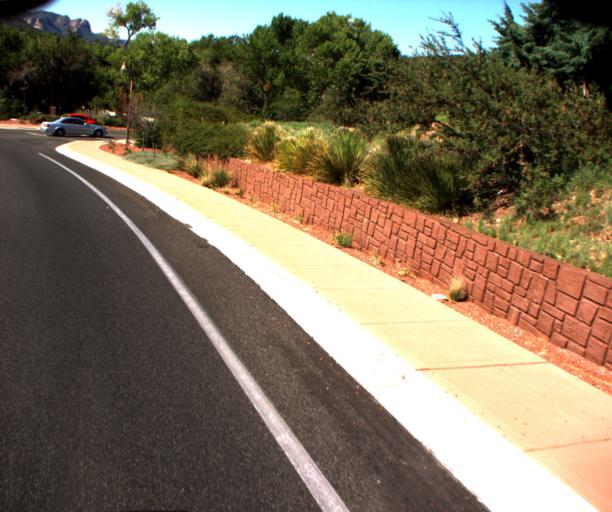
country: US
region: Arizona
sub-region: Coconino County
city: Sedona
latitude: 34.8641
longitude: -111.7639
